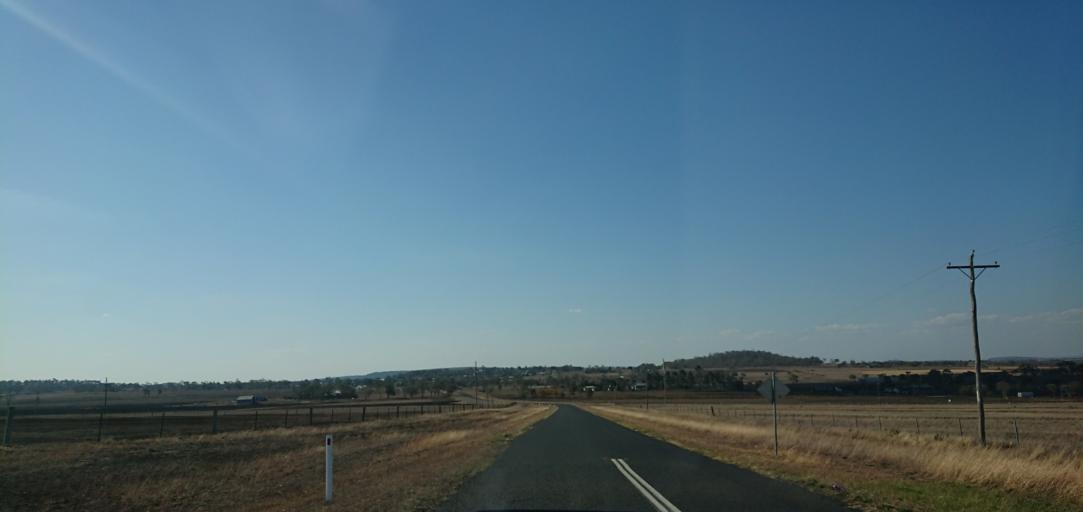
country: AU
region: Queensland
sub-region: Toowoomba
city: Westbrook
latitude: -27.6981
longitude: 151.7149
